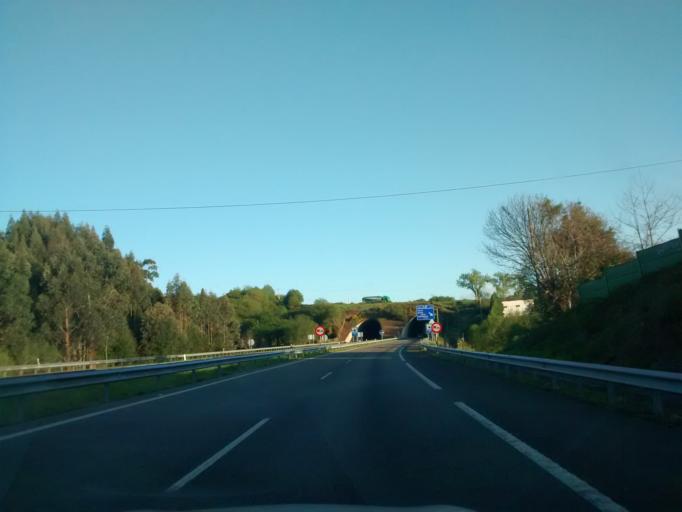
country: ES
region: Asturias
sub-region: Province of Asturias
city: Ribadesella
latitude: 43.4511
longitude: -5.1075
